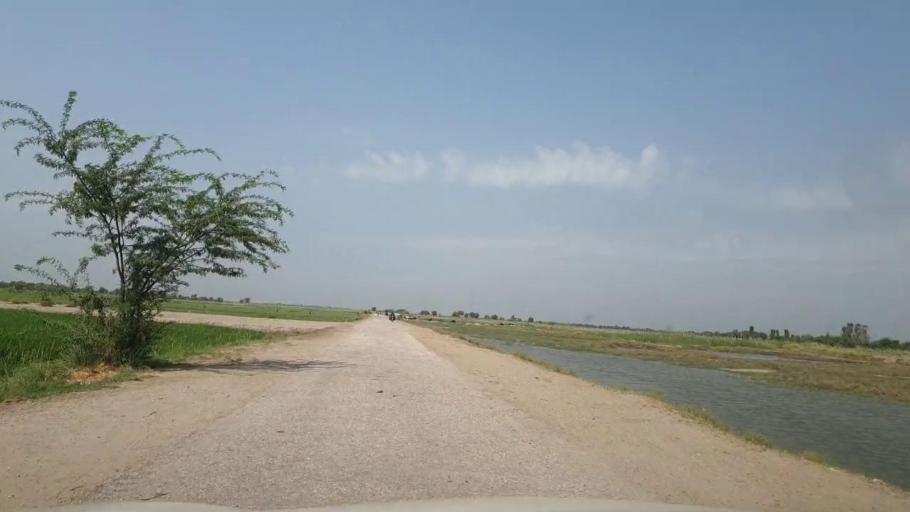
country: PK
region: Sindh
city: Ratodero
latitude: 27.8479
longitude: 68.2707
